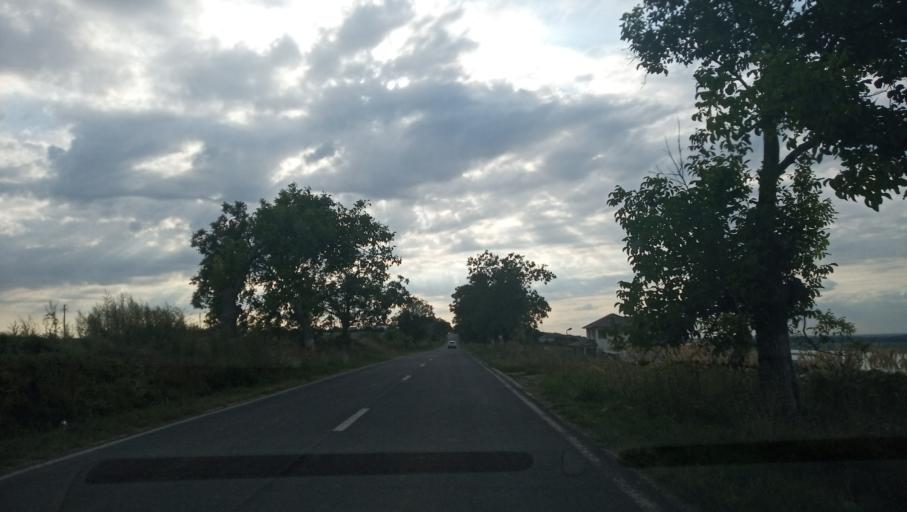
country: RO
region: Constanta
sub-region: Comuna Ostrov
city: Ostrov
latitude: 44.1020
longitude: 27.3838
